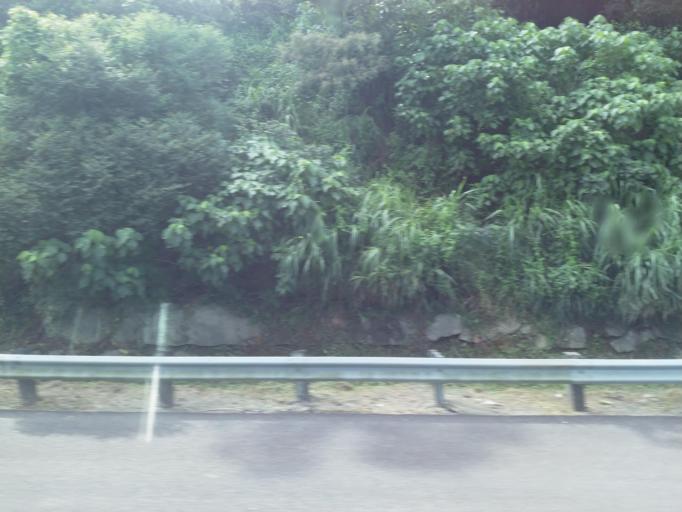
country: TW
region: Taiwan
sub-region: Pingtung
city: Pingtung
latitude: 22.7962
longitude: 120.4390
